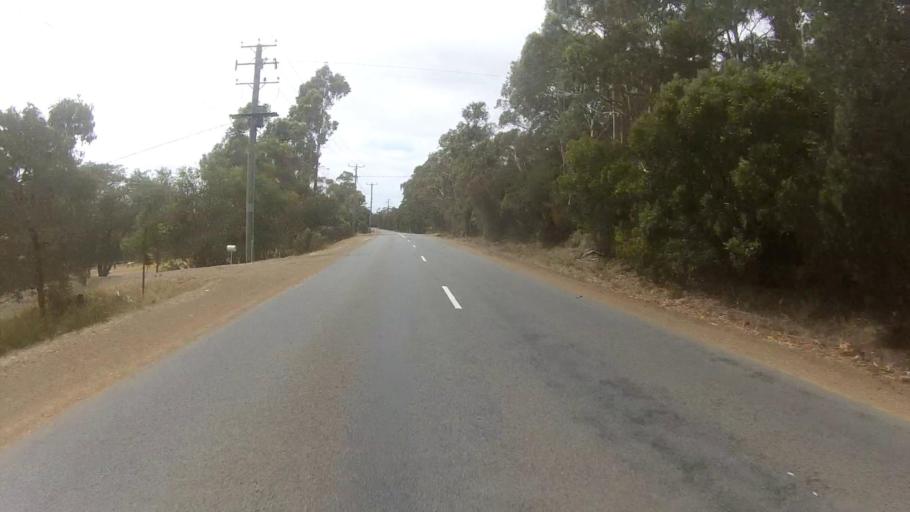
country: AU
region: Tasmania
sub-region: Kingborough
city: Margate
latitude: -43.0048
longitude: 147.2380
